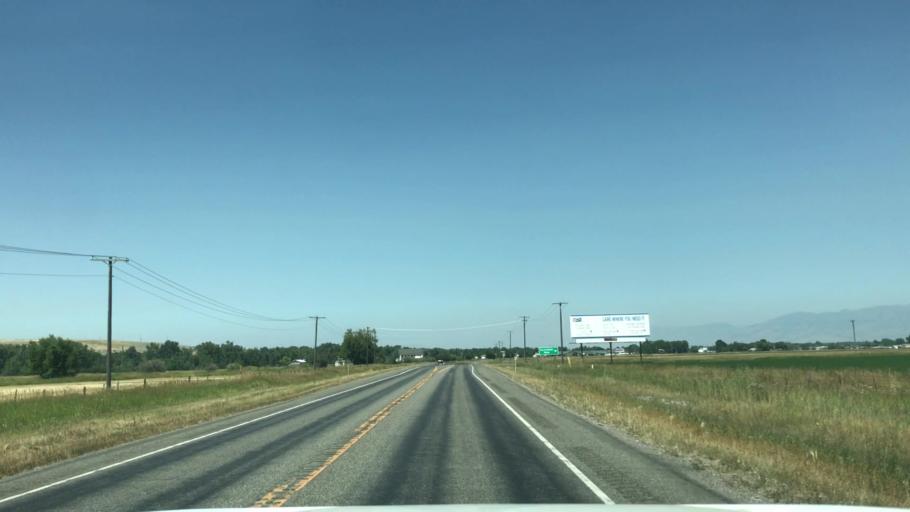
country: US
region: Montana
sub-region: Gallatin County
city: Four Corners
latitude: 45.6363
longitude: -111.1969
